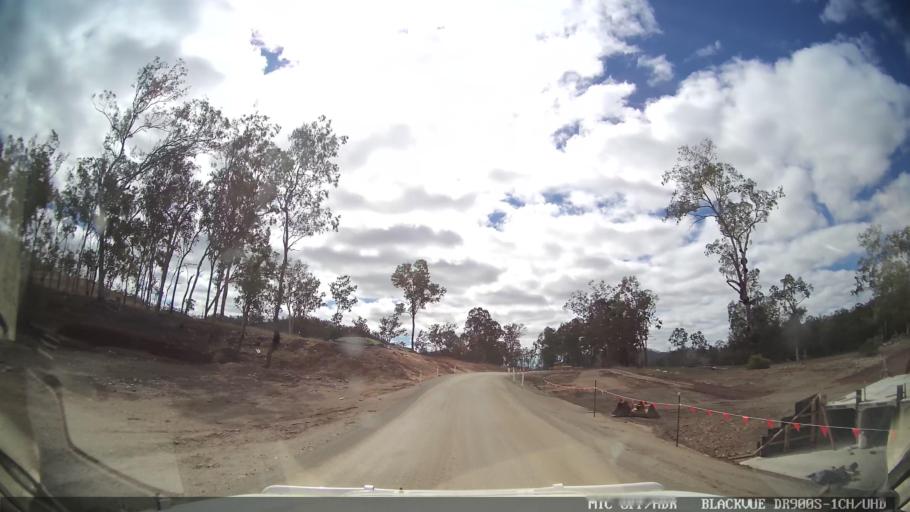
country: AU
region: Queensland
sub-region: Gladstone
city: Toolooa
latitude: -24.6142
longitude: 151.2993
